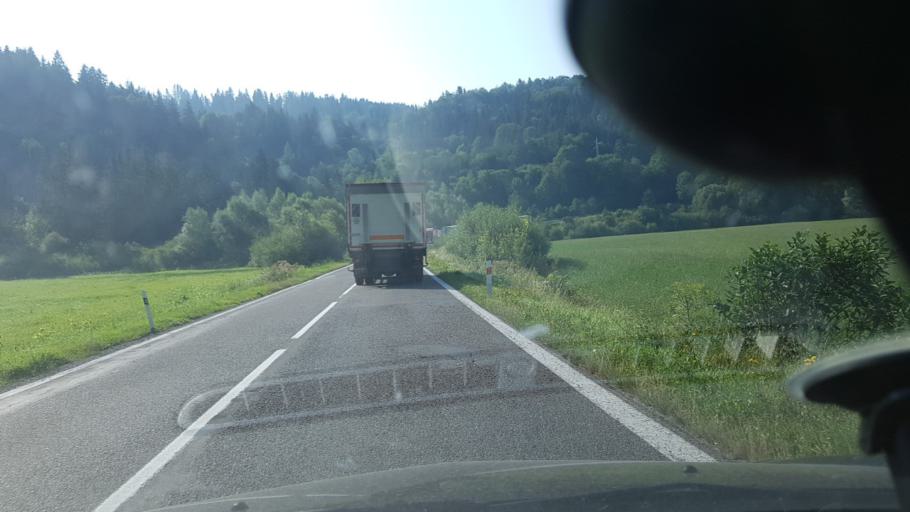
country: SK
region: Zilinsky
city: Tvrdosin
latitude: 49.2916
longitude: 19.4929
